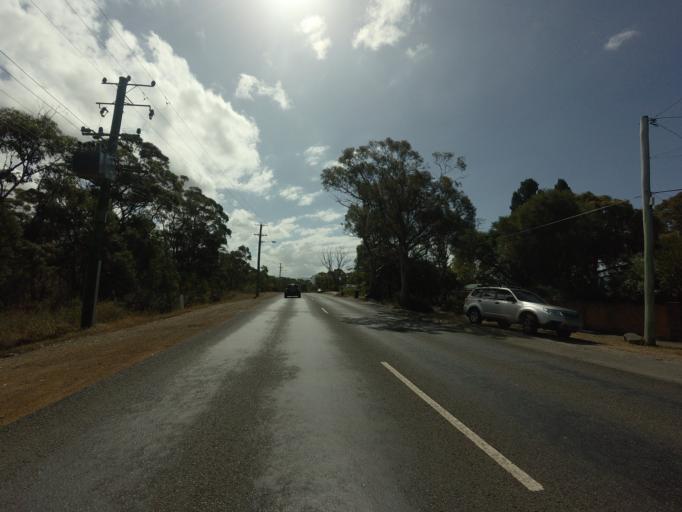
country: AU
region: Tasmania
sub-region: Hobart
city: Dynnyrne
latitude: -42.9156
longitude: 147.3167
